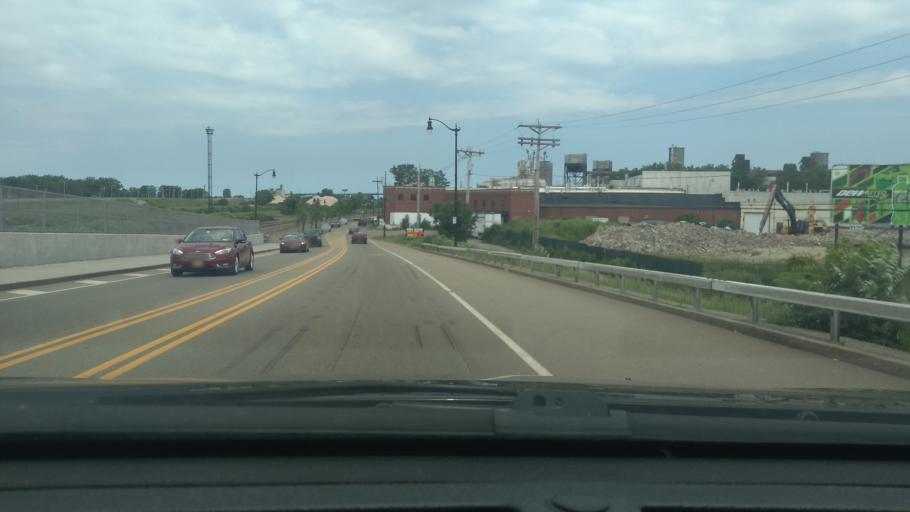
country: US
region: New York
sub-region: Erie County
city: Buffalo
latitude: 42.8564
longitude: -78.8655
